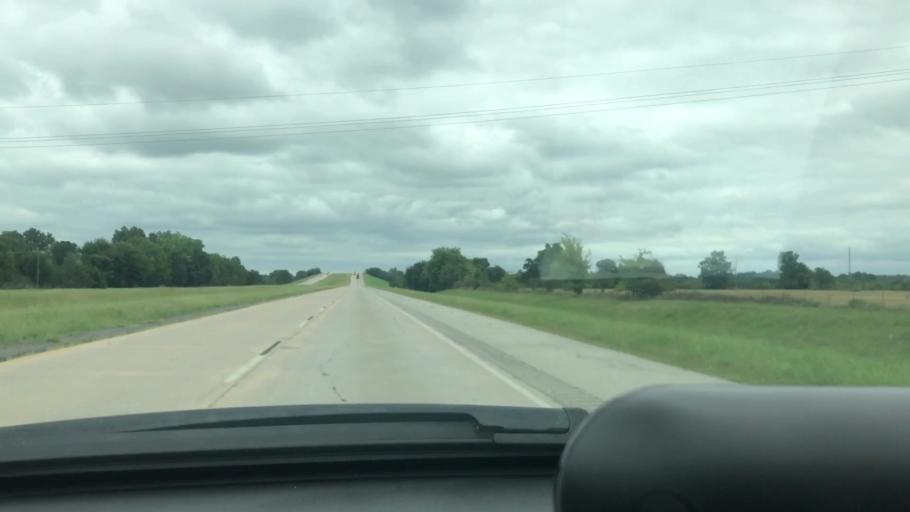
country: US
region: Oklahoma
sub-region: Wagoner County
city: Wagoner
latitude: 35.8750
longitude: -95.4019
